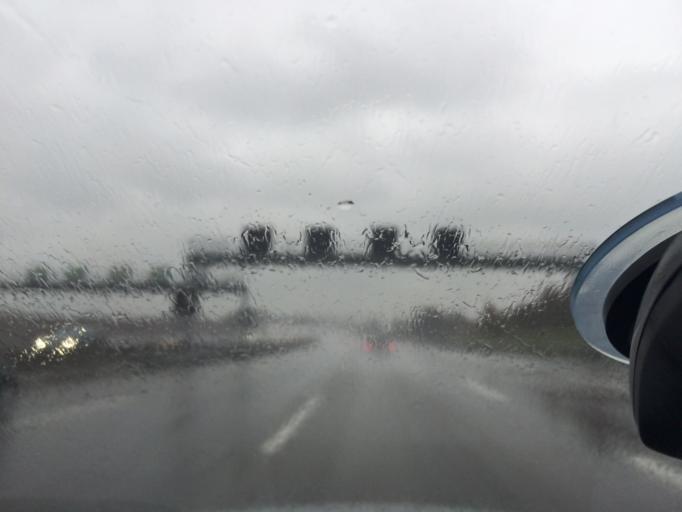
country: DE
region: Hesse
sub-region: Regierungsbezirk Darmstadt
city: Bad Homburg vor der Hoehe
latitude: 50.2056
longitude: 8.6535
